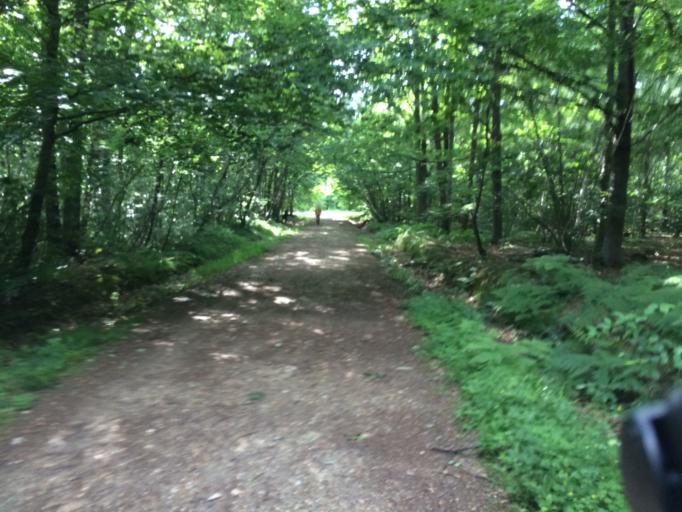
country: FR
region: Ile-de-France
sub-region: Departement de l'Essonne
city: Igny
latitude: 48.7515
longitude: 2.2423
